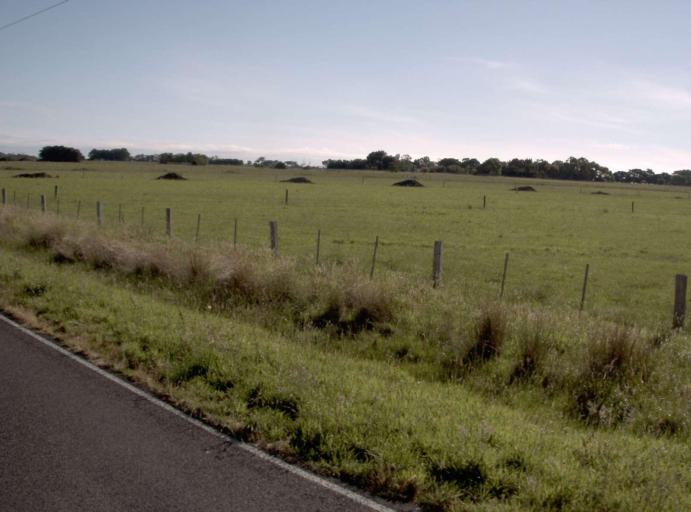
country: AU
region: Victoria
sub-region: Latrobe
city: Morwell
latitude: -38.6824
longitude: 146.3900
